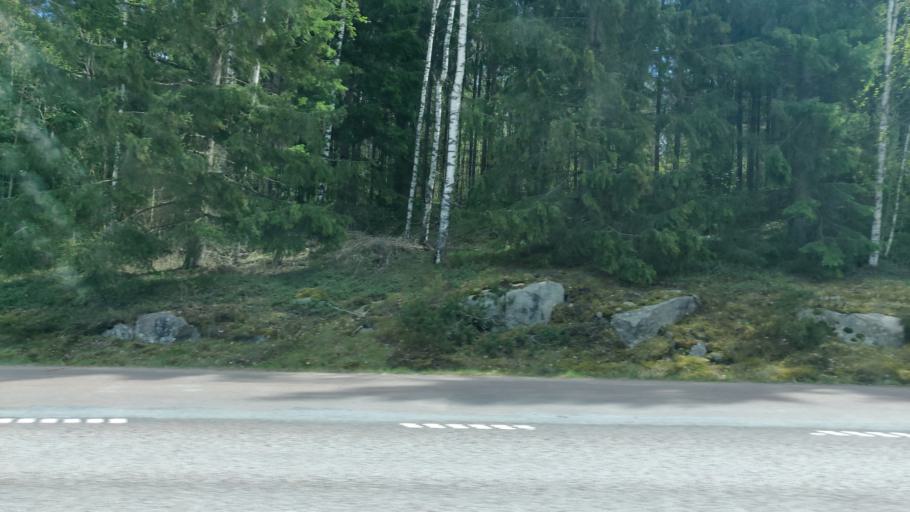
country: SE
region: Vaermland
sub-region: Karlstads Kommun
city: Molkom
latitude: 59.5389
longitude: 13.6199
